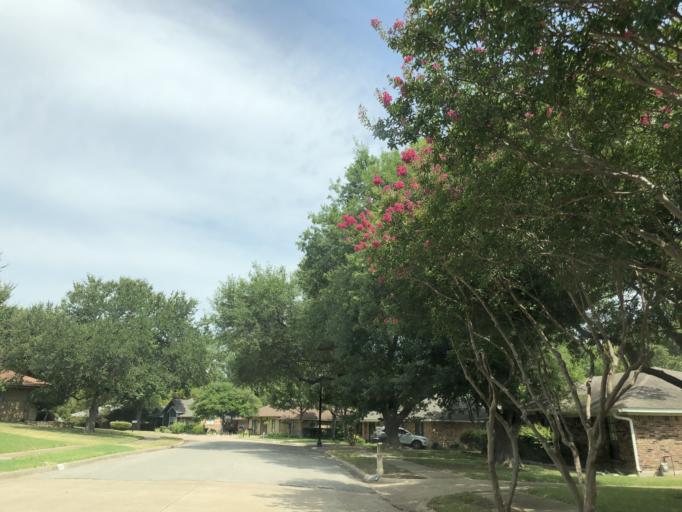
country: US
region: Texas
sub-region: Dallas County
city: Garland
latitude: 32.8549
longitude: -96.6193
